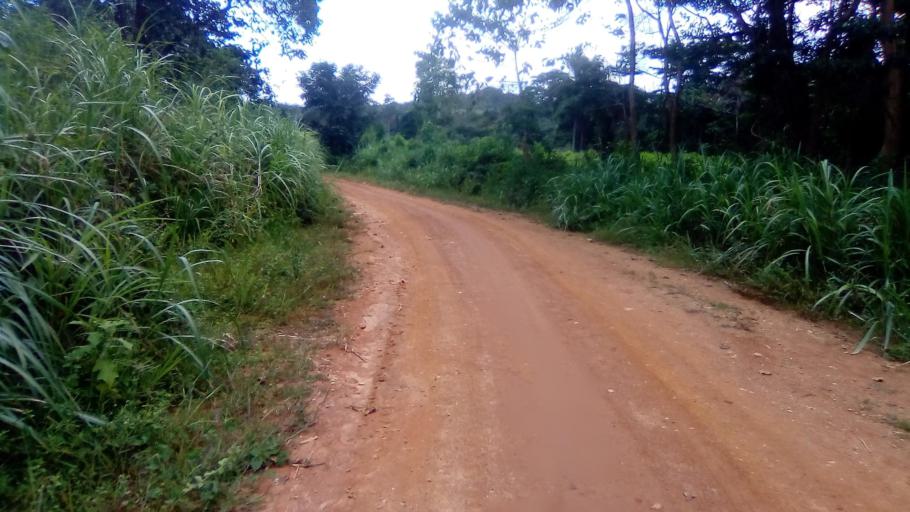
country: SL
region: Eastern Province
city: Simbakoro
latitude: 8.5472
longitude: -10.9326
